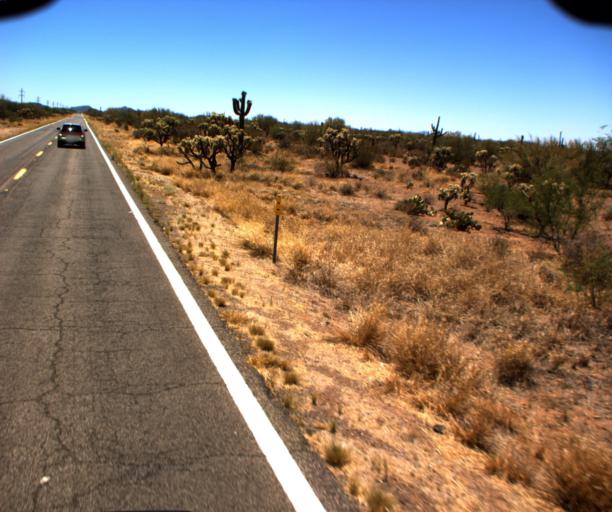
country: US
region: Arizona
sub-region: Pima County
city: Sells
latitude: 32.0399
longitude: -112.0172
